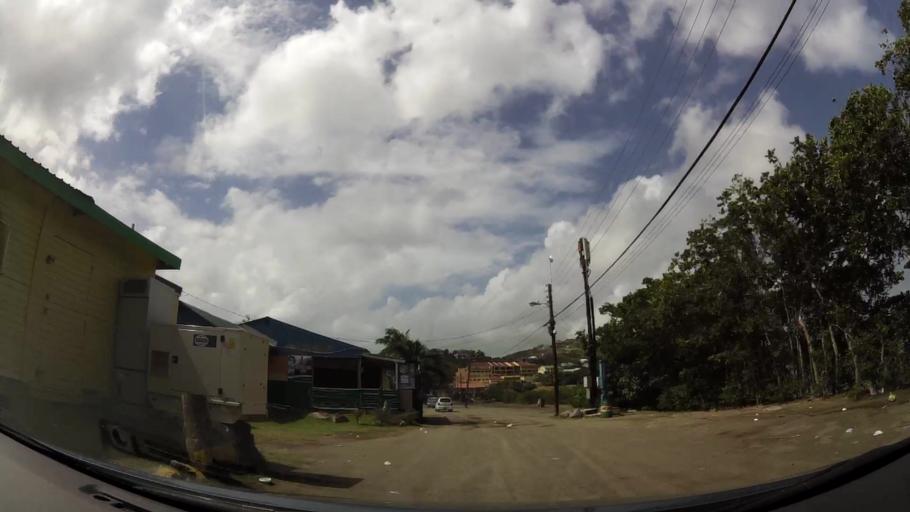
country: KN
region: Saint George Basseterre
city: Basseterre
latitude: 17.2813
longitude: -62.6881
